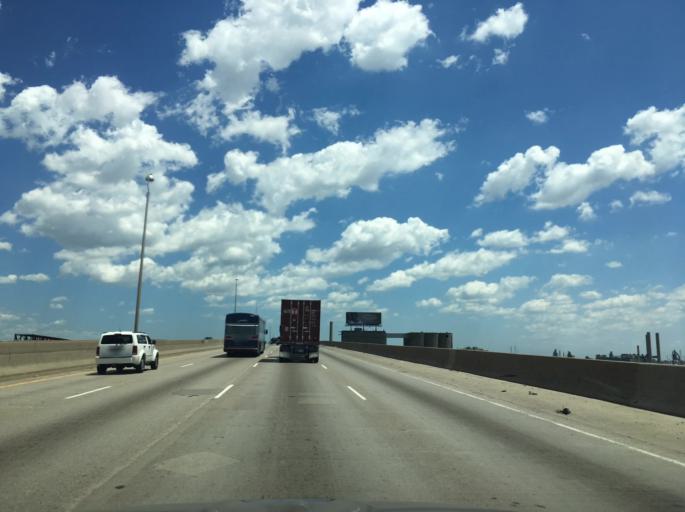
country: US
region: Michigan
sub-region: Wayne County
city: River Rouge
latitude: 42.2857
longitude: -83.1423
